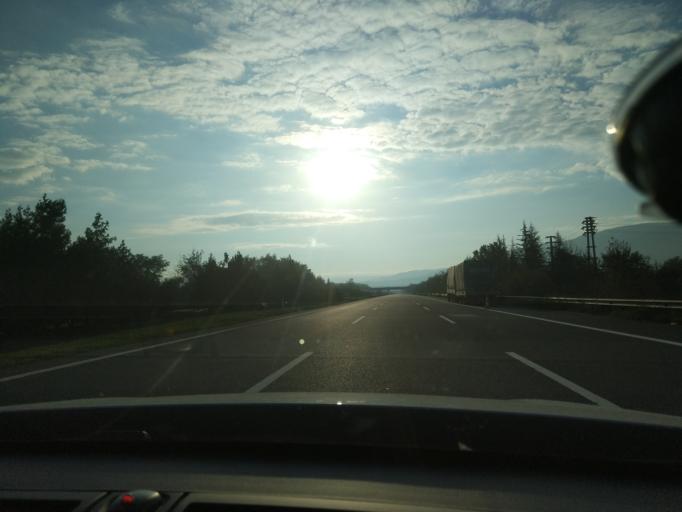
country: TR
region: Duzce
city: Duzce
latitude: 40.8006
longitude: 31.1811
